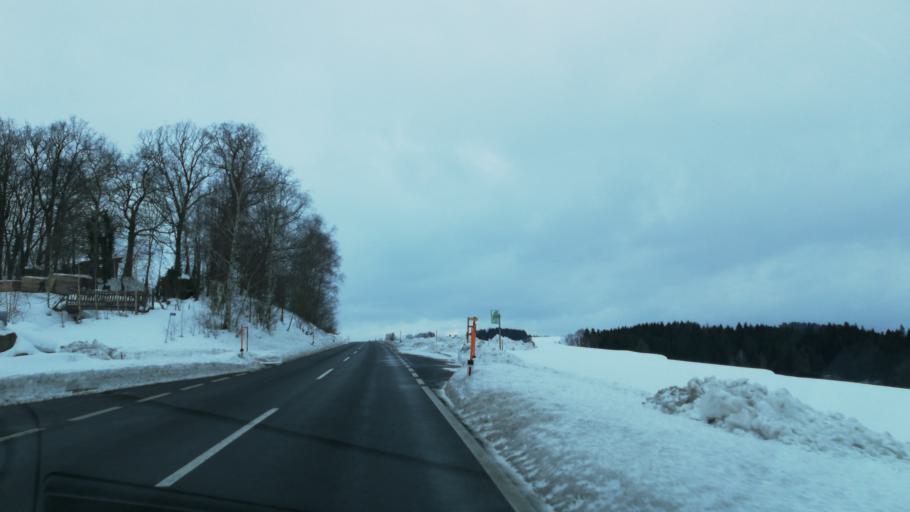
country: AT
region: Upper Austria
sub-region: Politischer Bezirk Urfahr-Umgebung
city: Herzogsdorf
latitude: 48.4597
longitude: 14.1235
